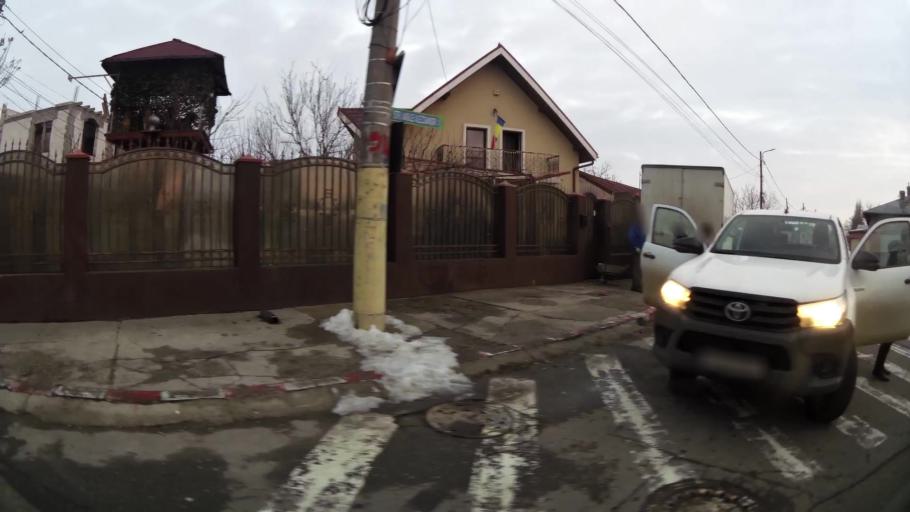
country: RO
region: Ilfov
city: Dobroesti
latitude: 44.4536
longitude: 26.1810
